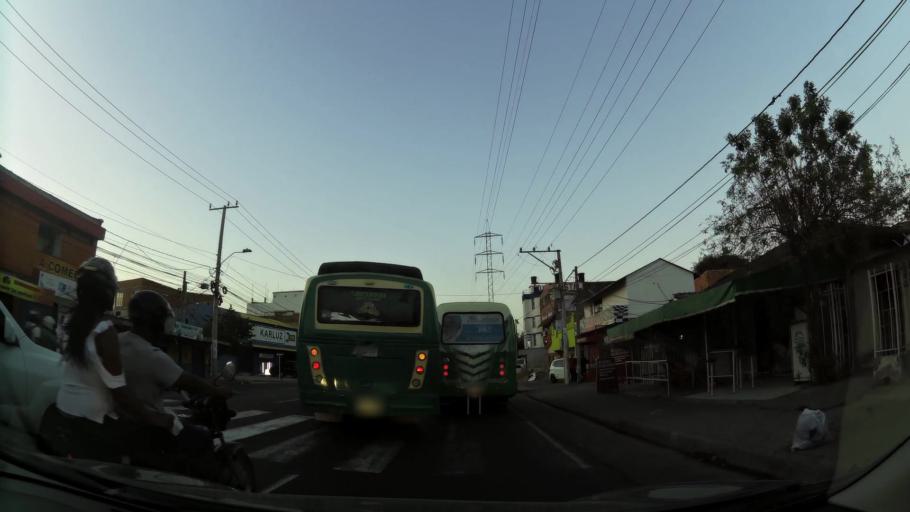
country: CO
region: Bolivar
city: Cartagena
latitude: 10.4031
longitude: -75.5198
